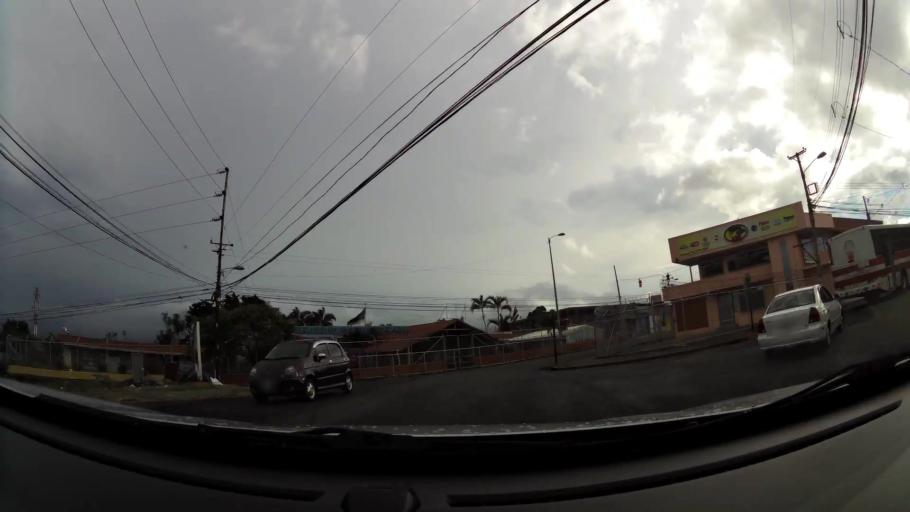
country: CR
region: San Jose
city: Colima
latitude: 9.9418
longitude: -84.0933
